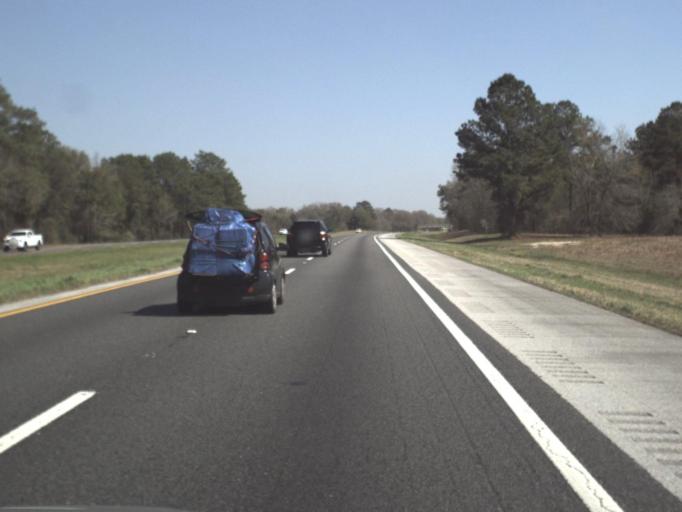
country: US
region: Florida
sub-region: Jackson County
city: Marianna
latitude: 30.6803
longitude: -85.0895
